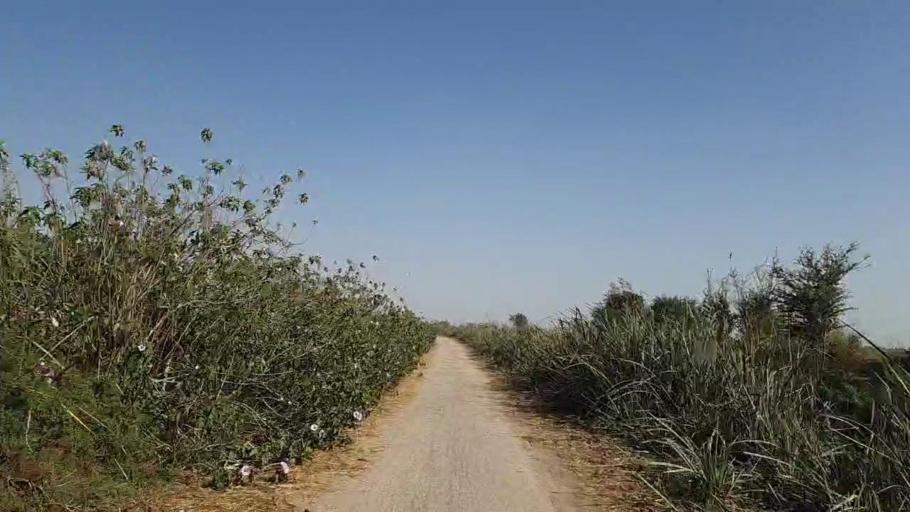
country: PK
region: Sindh
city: Chuhar Jamali
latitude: 24.4833
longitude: 68.0991
